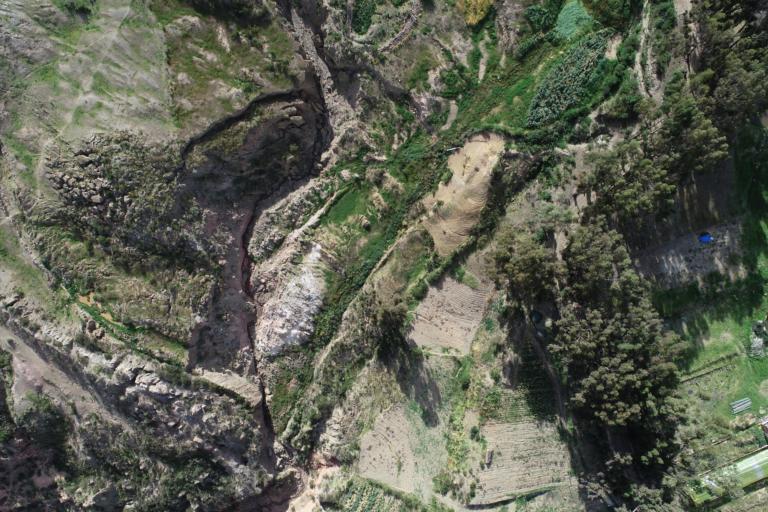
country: BO
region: La Paz
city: La Paz
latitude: -16.5508
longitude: -67.9939
